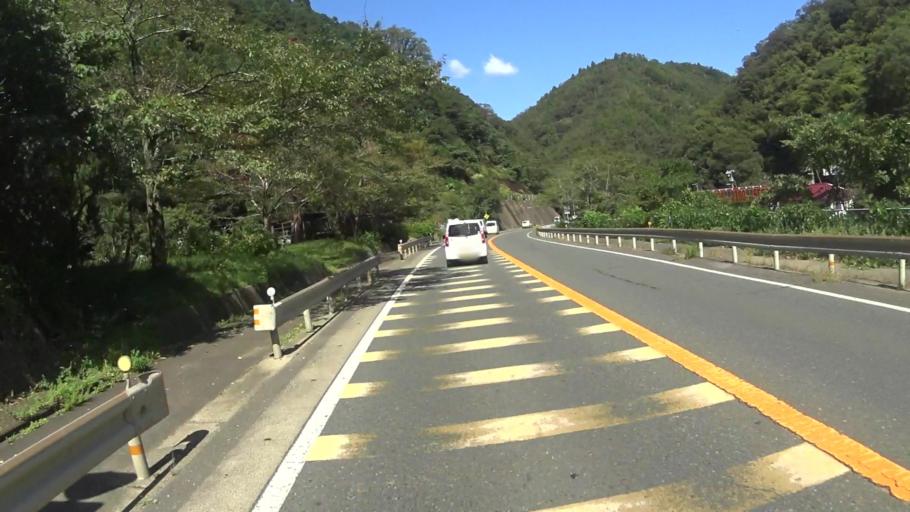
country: JP
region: Kyoto
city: Maizuru
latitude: 35.3826
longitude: 135.3140
